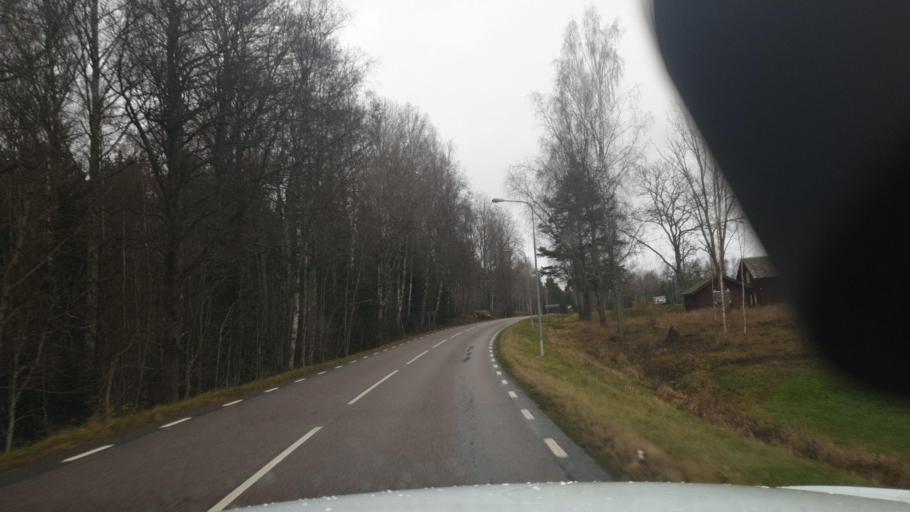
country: SE
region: Vaermland
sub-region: Arvika Kommun
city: Arvika
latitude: 59.4880
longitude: 12.6872
